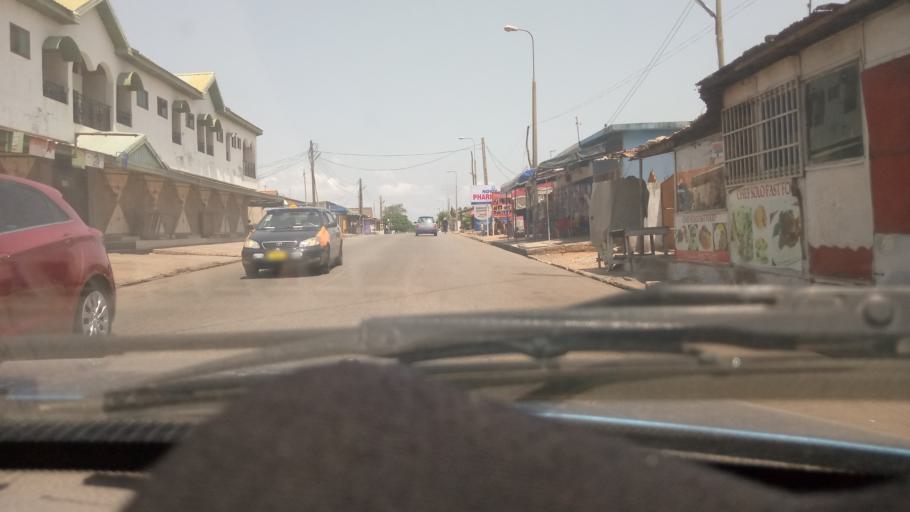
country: GH
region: Greater Accra
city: Accra
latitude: 5.5345
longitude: -0.2377
